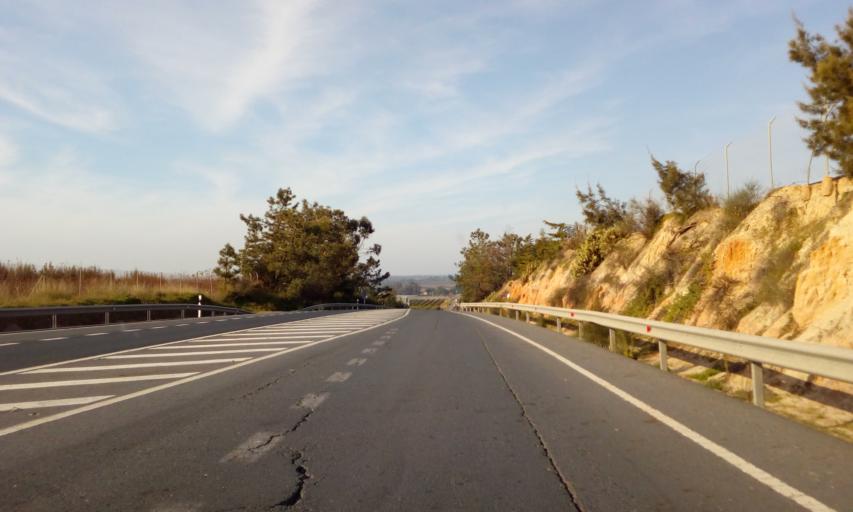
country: ES
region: Andalusia
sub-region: Provincia de Huelva
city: Lepe
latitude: 37.2525
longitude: -7.2428
